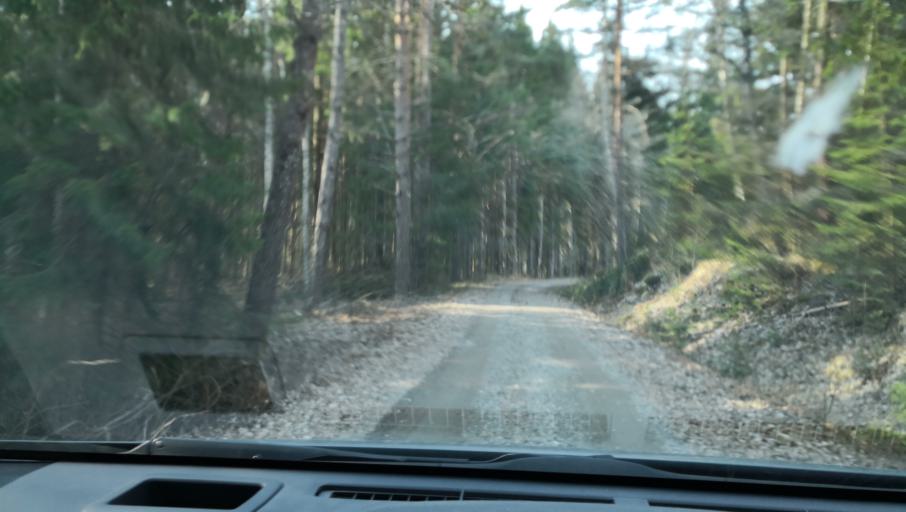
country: SE
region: OErebro
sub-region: Lindesbergs Kommun
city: Frovi
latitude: 59.3857
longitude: 15.4053
